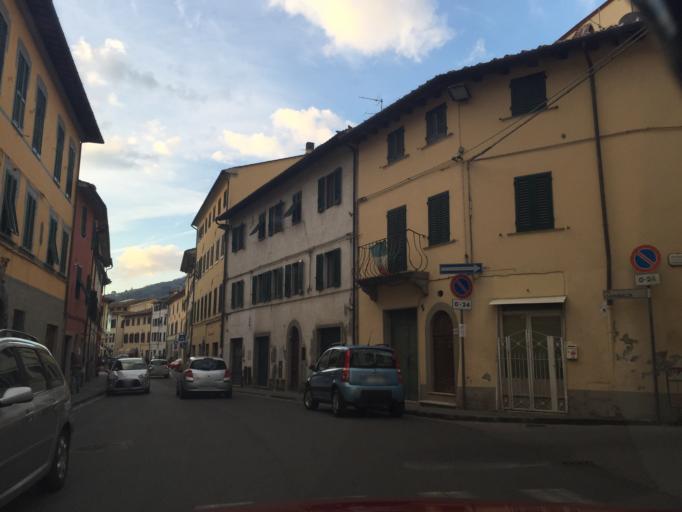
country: IT
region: Tuscany
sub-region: Provincia di Pistoia
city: Borgo a Buggiano
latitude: 43.8785
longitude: 10.7306
